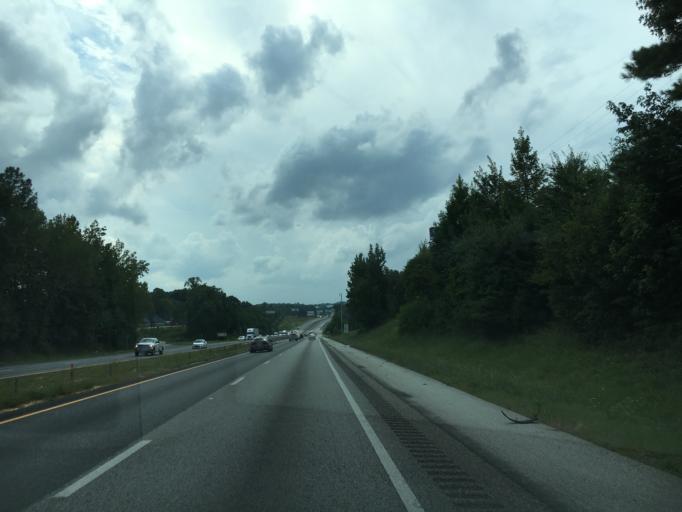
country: US
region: South Carolina
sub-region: Cherokee County
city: Gaffney
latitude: 35.0792
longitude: -81.7173
